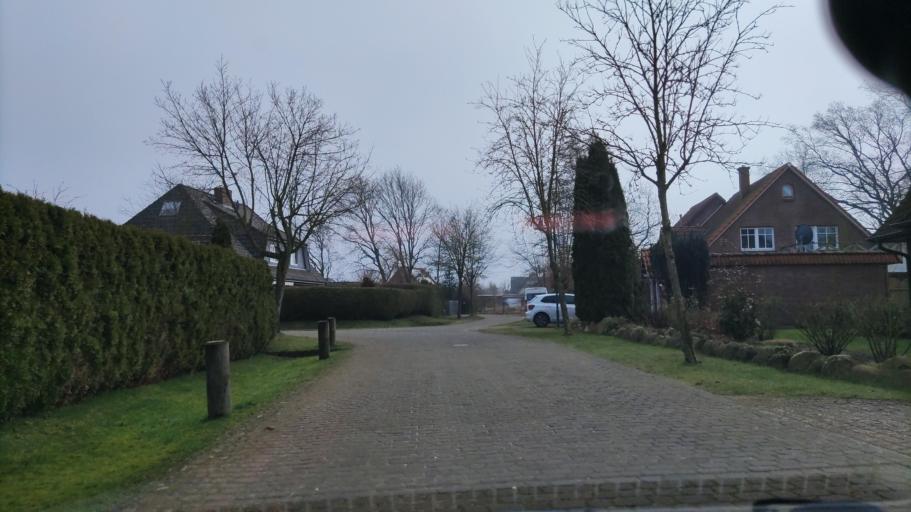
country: DE
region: Schleswig-Holstein
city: Lauenburg
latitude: 53.3503
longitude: 10.5569
